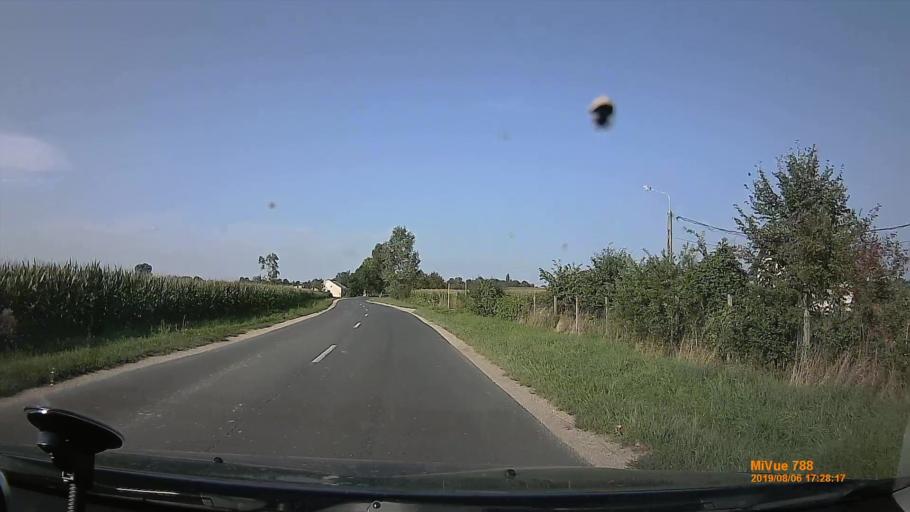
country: HR
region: Medimurska
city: Kotoriba
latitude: 46.3907
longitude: 16.8388
